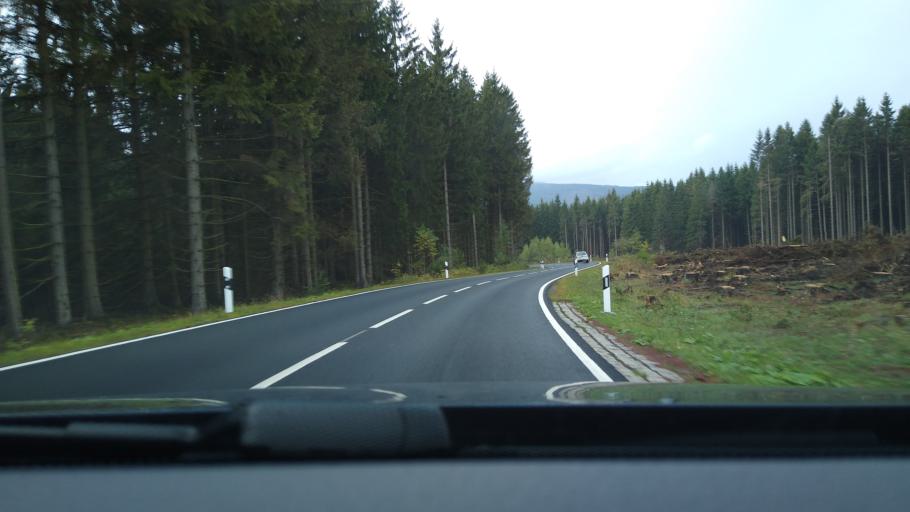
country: DE
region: Saxony-Anhalt
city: Elbingerode
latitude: 51.7719
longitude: 10.7489
